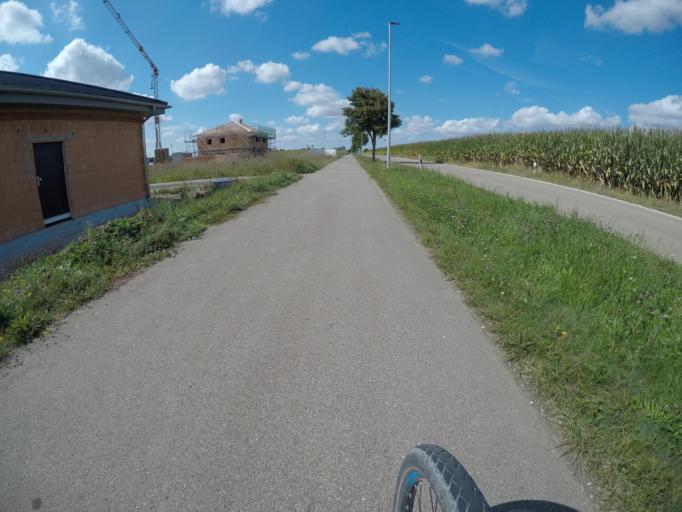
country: DE
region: Bavaria
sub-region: Swabia
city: Hochstadt an der Donau
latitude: 48.6204
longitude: 10.5517
